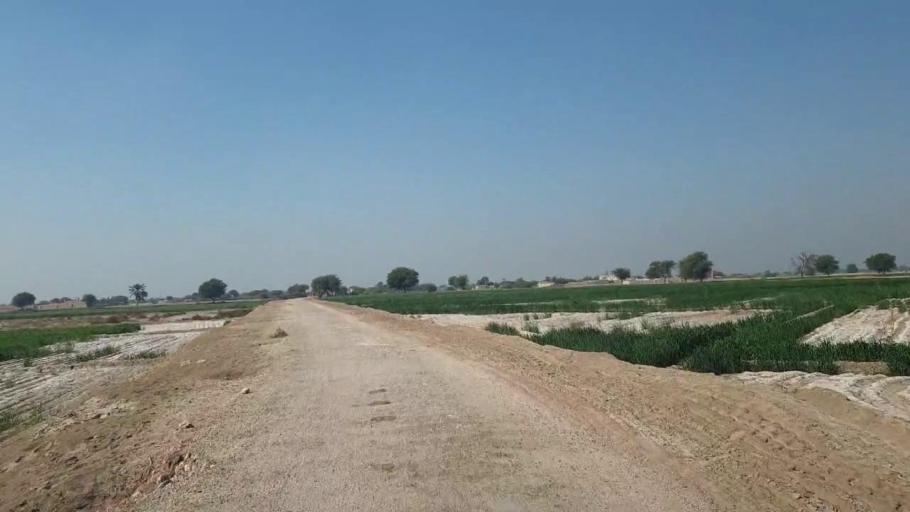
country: PK
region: Sindh
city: Shahpur Chakar
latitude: 26.1182
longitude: 68.6095
